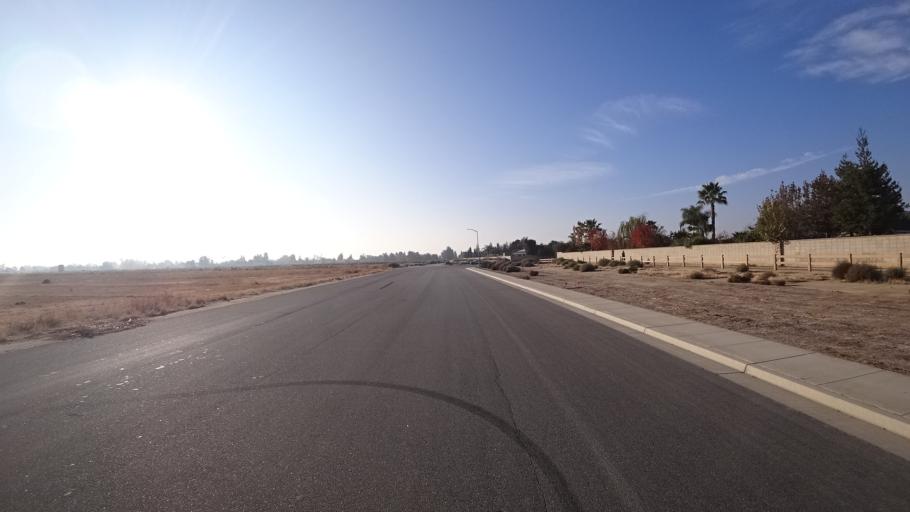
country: US
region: California
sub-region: Kern County
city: Rosedale
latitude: 35.3699
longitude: -119.1722
